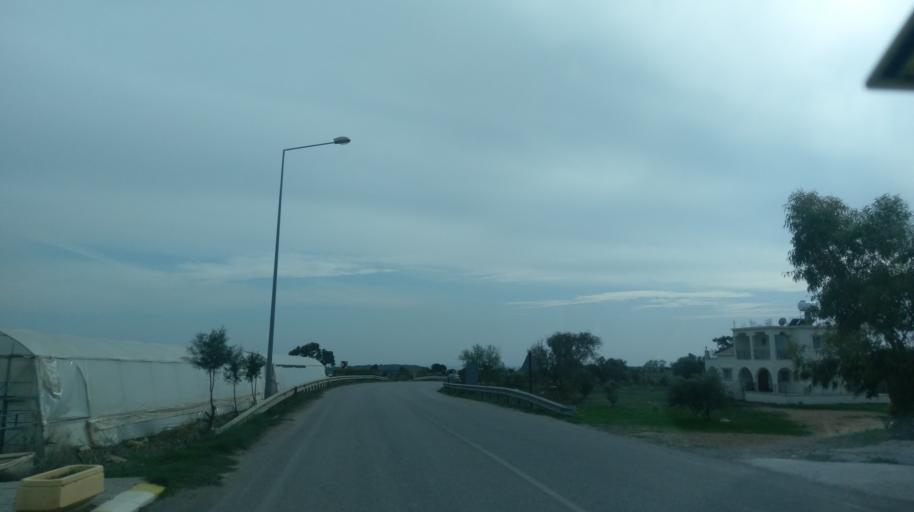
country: CY
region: Ammochostos
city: Leonarisso
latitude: 35.4708
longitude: 34.1452
